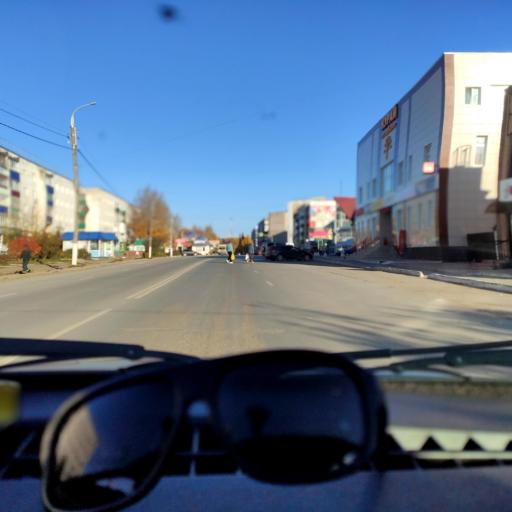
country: RU
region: Bashkortostan
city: Blagoveshchensk
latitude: 55.0478
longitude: 55.9568
